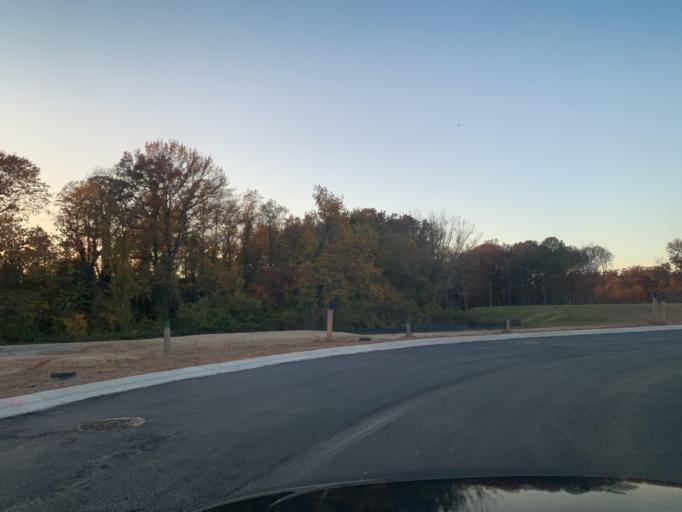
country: US
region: Maryland
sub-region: Baltimore County
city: Middle River
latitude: 39.3143
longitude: -76.4350
